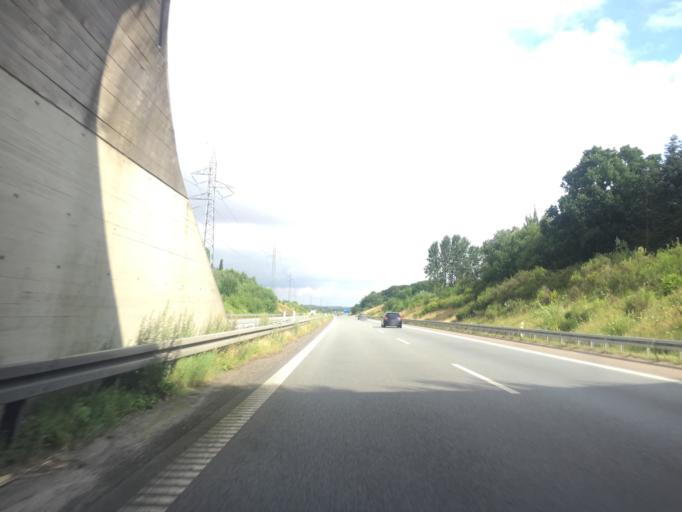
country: DK
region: South Denmark
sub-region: Svendborg Kommune
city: Svendborg
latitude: 55.0998
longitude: 10.5681
